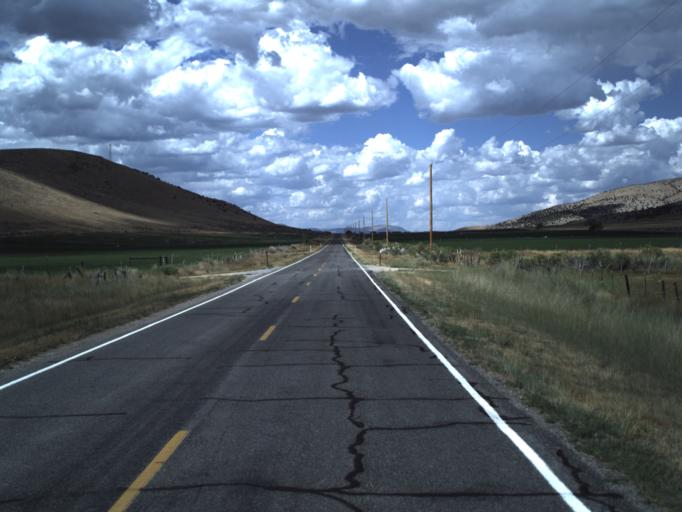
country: US
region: Utah
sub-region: Sanpete County
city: Gunnison
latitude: 39.1379
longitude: -111.7102
